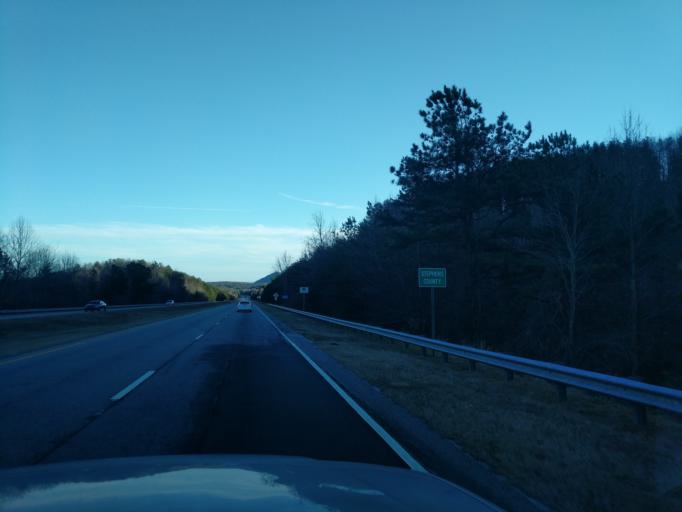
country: US
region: Georgia
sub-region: Stephens County
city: Toccoa
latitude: 34.5831
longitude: -83.4107
